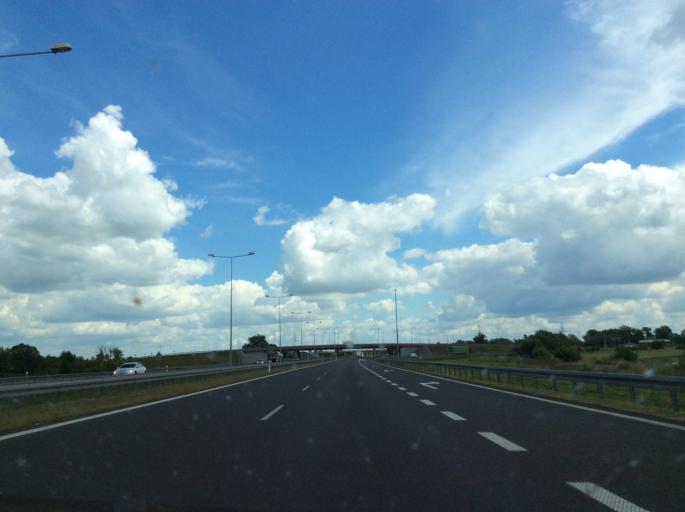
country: PL
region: Greater Poland Voivodeship
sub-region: Powiat turecki
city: Brudzew
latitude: 52.1412
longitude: 18.6019
